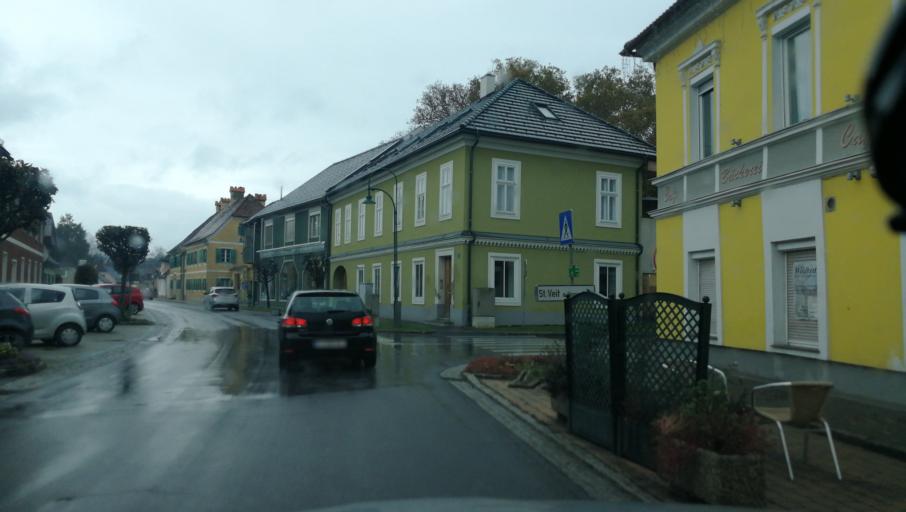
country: AT
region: Styria
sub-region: Politischer Bezirk Leibnitz
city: Strass in Steiermark
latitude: 46.7283
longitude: 15.6208
